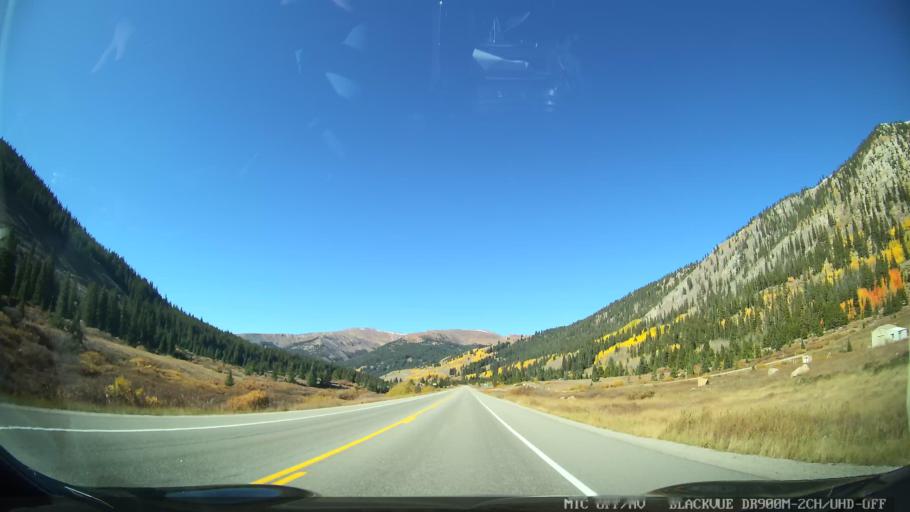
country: US
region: Colorado
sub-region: Lake County
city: Leadville
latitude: 39.3617
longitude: -106.1939
